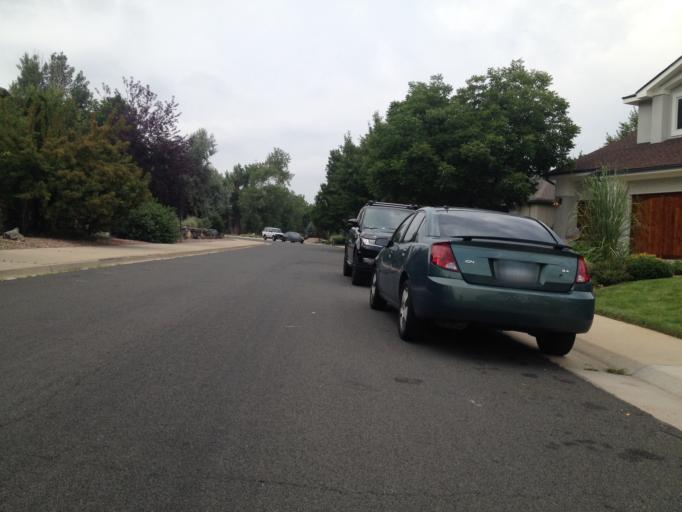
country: US
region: Colorado
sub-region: Boulder County
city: Louisville
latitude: 39.9613
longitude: -105.1426
